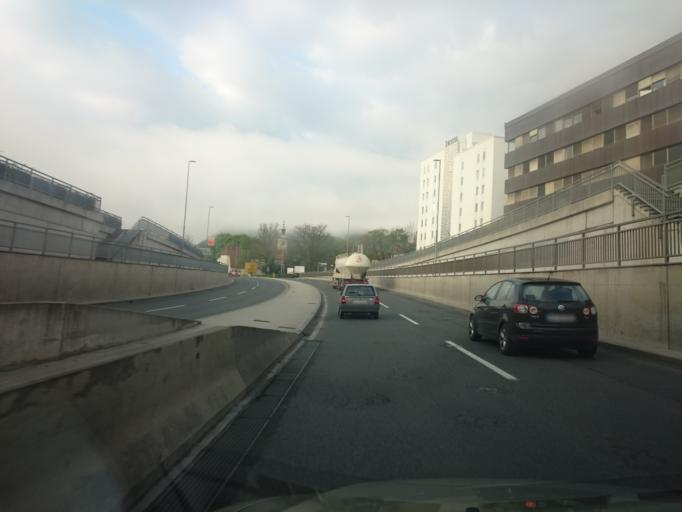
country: SI
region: Celje
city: Celje
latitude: 46.2338
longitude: 15.2684
